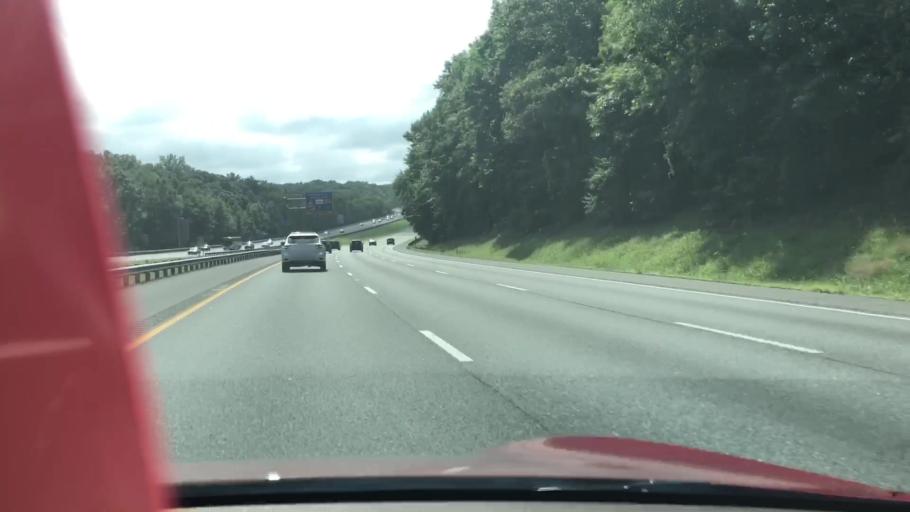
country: US
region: Maryland
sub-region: Harford County
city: Perryman
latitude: 39.5063
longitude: -76.2164
